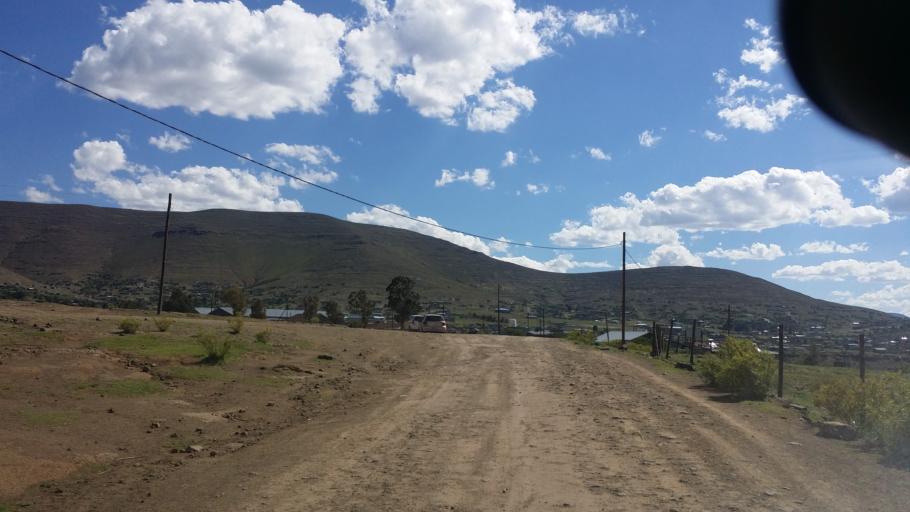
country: LS
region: Mokhotlong
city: Mokhotlong
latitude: -29.2777
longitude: 29.0665
